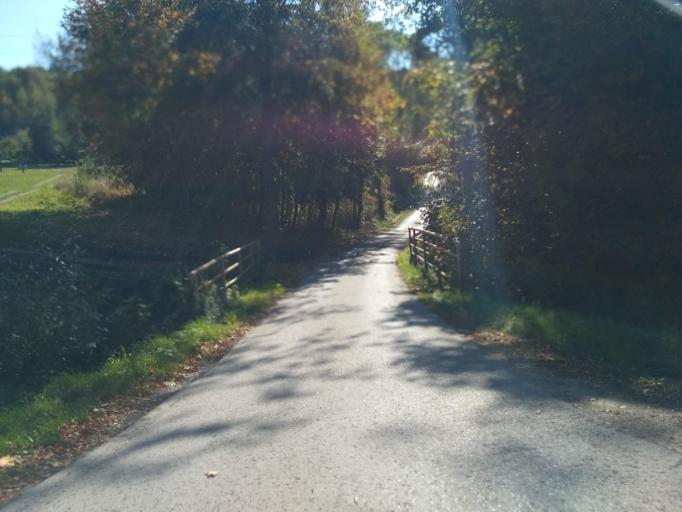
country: PL
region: Subcarpathian Voivodeship
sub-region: Powiat debicki
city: Slotowa
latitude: 49.9406
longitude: 21.2813
